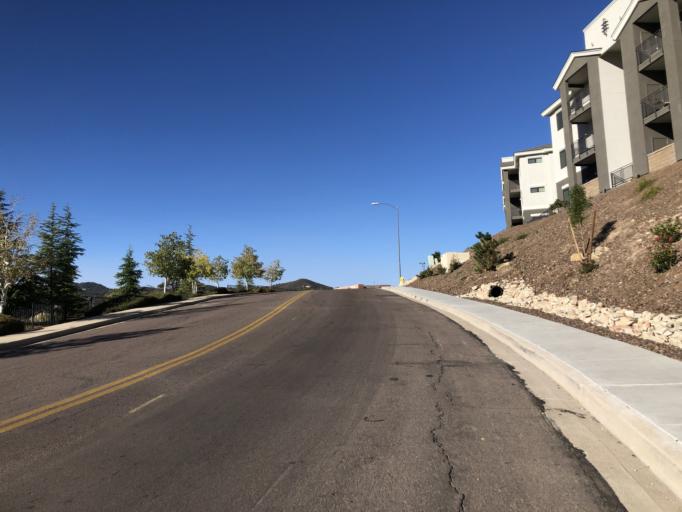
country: US
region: Arizona
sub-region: Yavapai County
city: Prescott
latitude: 34.5498
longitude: -112.4013
